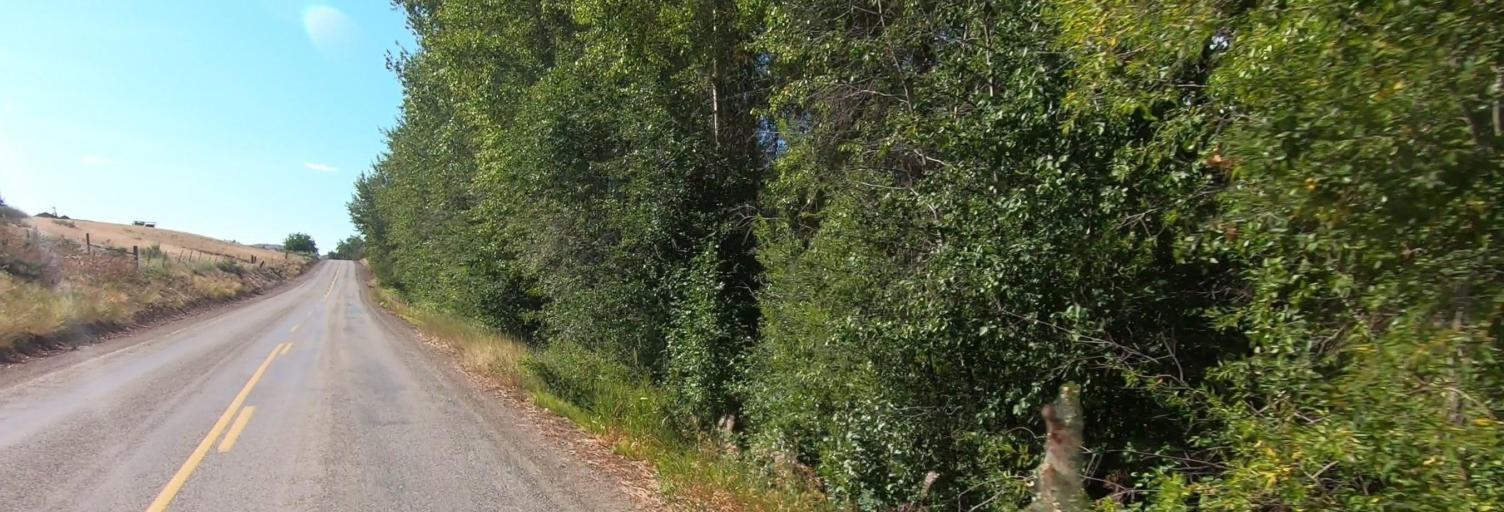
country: US
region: Washington
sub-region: Okanogan County
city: Brewster
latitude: 48.5264
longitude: -120.1779
